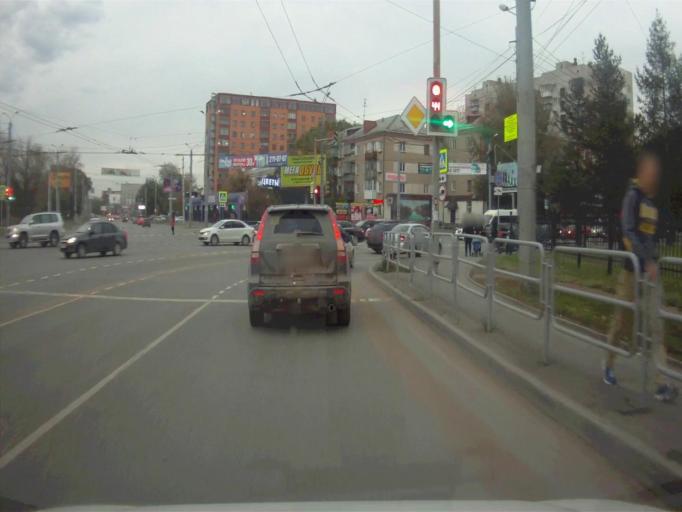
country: RU
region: Chelyabinsk
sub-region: Gorod Chelyabinsk
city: Chelyabinsk
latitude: 55.1676
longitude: 61.3799
